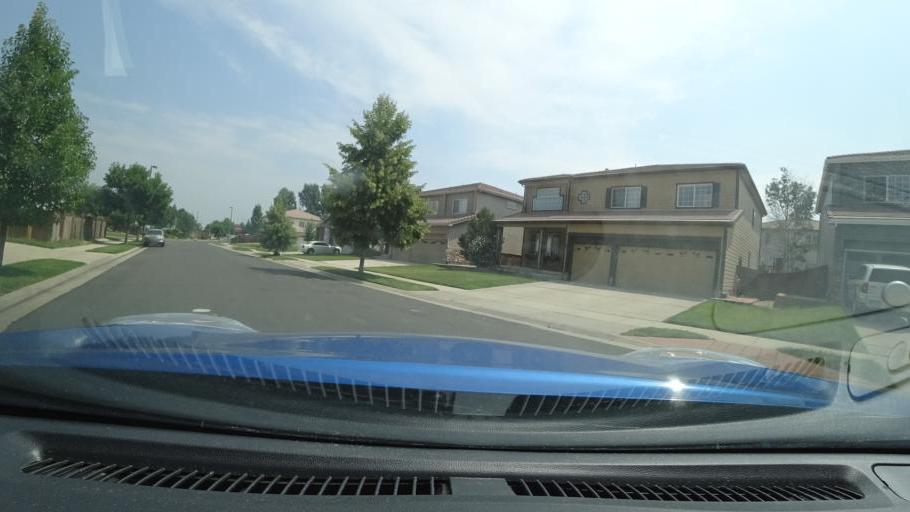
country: US
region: Colorado
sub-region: Adams County
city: Aurora
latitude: 39.7800
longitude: -104.7542
